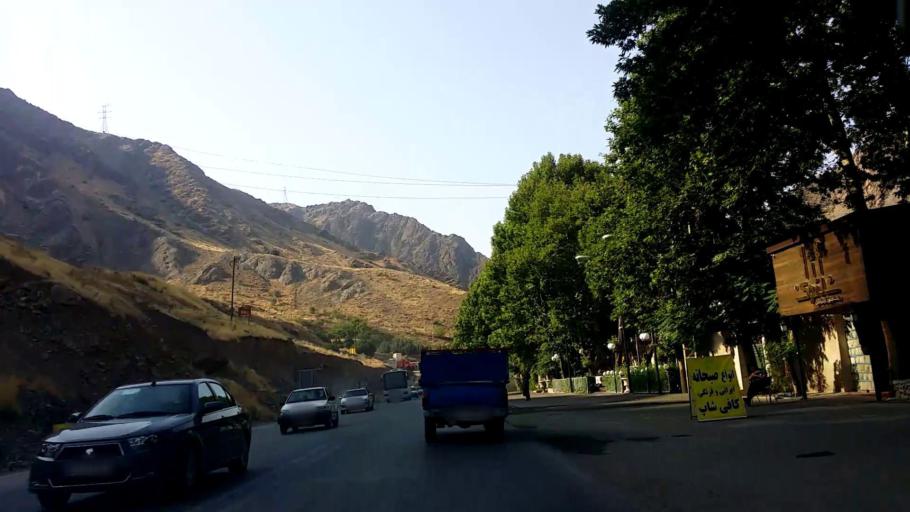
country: IR
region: Alborz
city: Karaj
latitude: 35.9046
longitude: 51.0437
